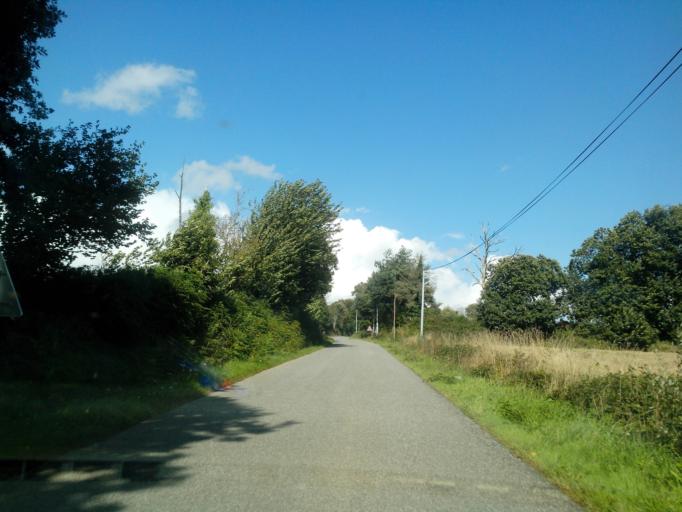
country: FR
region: Brittany
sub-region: Departement des Cotes-d'Armor
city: Merdrignac
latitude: 48.1595
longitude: -2.4194
